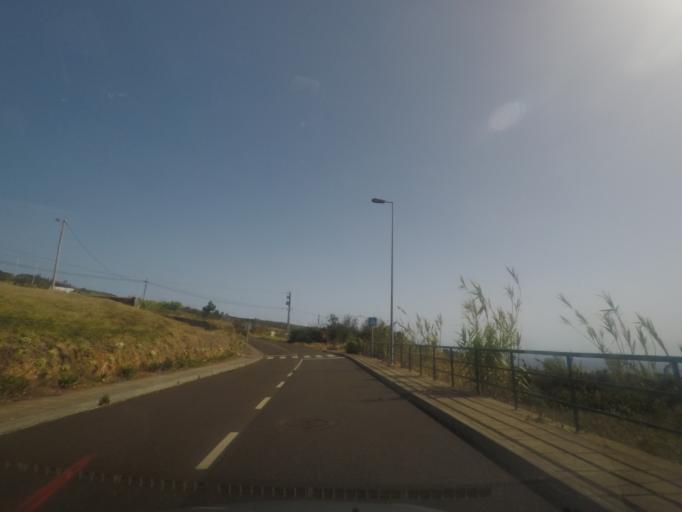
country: PT
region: Madeira
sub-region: Calheta
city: Faja da Ovelha
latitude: 32.8123
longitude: -17.2524
